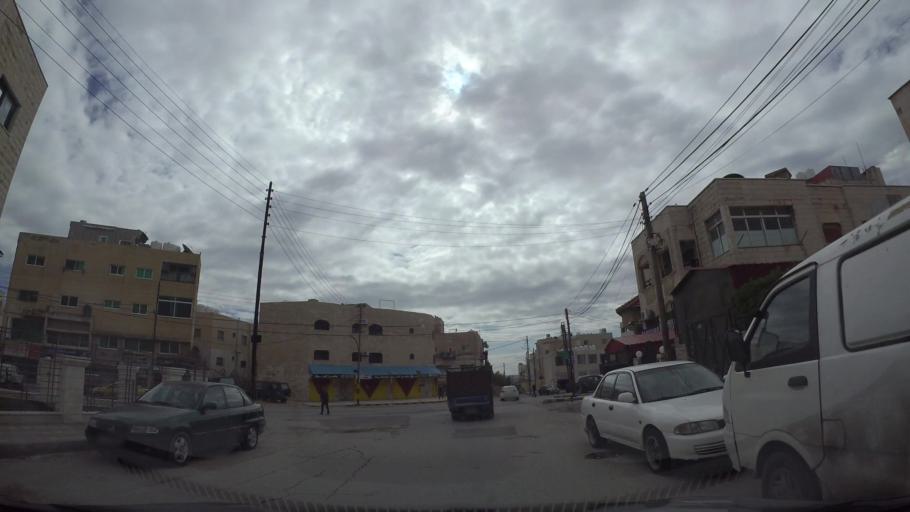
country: JO
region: Amman
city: Wadi as Sir
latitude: 31.9485
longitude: 35.8398
